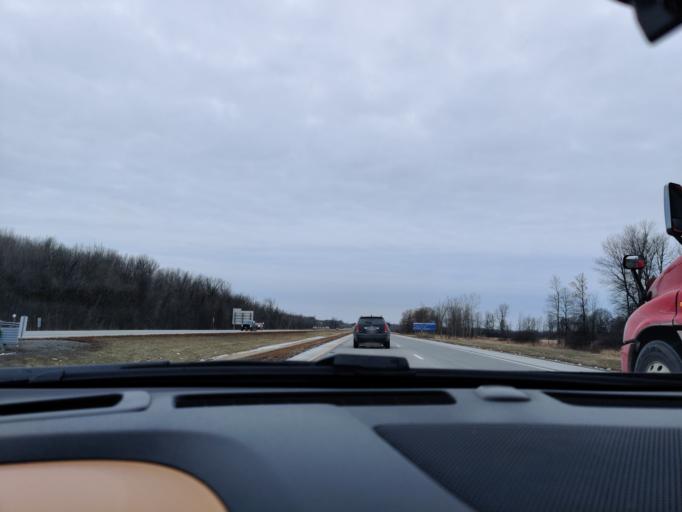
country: US
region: New York
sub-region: St. Lawrence County
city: Ogdensburg
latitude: 44.8696
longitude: -75.3071
